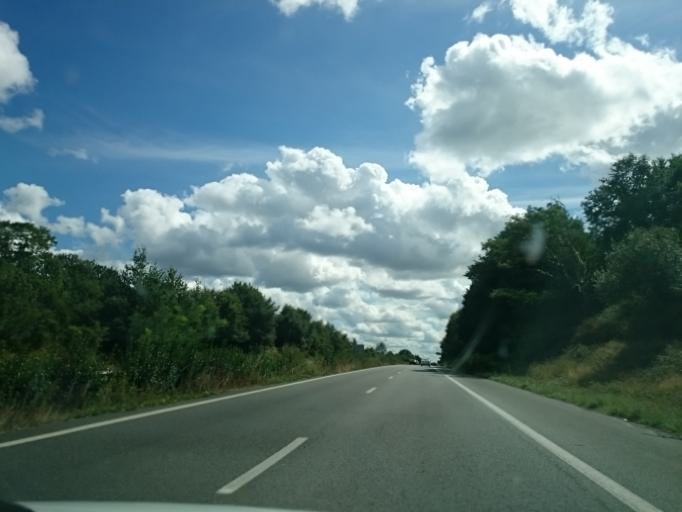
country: FR
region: Pays de la Loire
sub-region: Departement de la Loire-Atlantique
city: Carquefou
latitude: 47.2787
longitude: -1.4797
